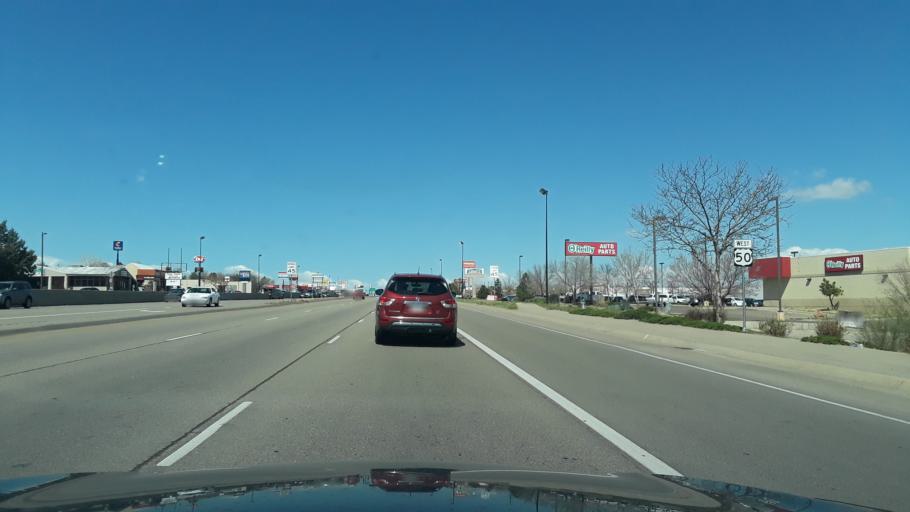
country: US
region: Colorado
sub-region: Pueblo County
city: Pueblo
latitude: 38.3083
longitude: -104.6217
